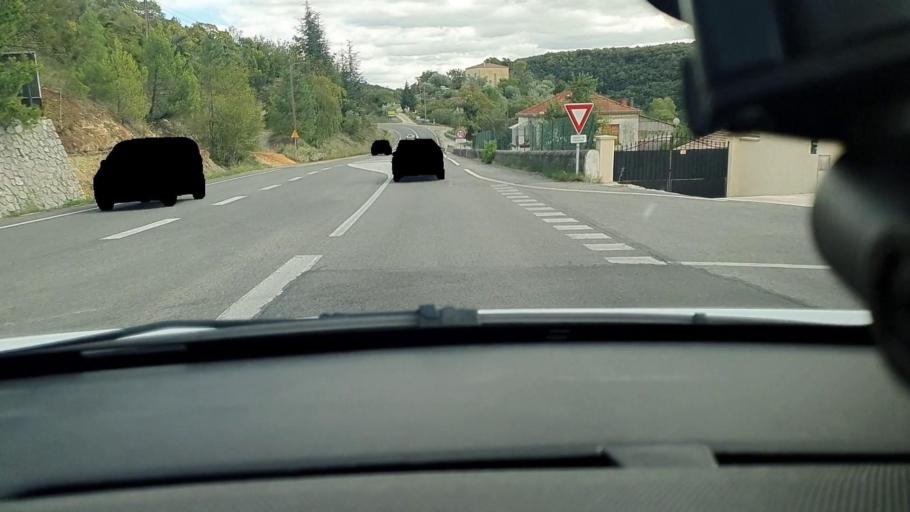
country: FR
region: Languedoc-Roussillon
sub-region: Departement du Gard
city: Les Mages
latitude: 44.2304
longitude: 4.1478
